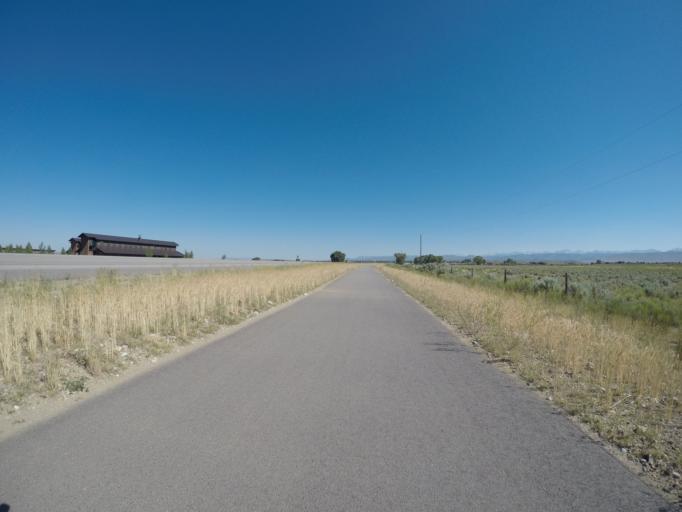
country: US
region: Wyoming
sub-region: Sublette County
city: Pinedale
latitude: 42.8307
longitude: -109.8461
